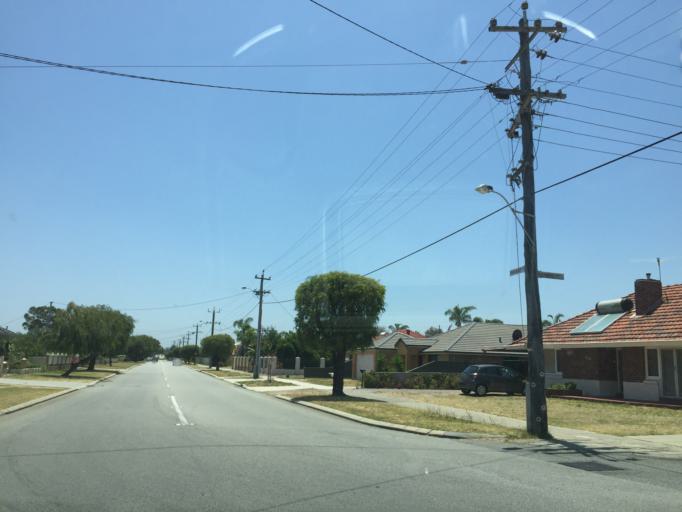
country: AU
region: Western Australia
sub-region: Canning
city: Queens Park
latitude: -32.0081
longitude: 115.9422
